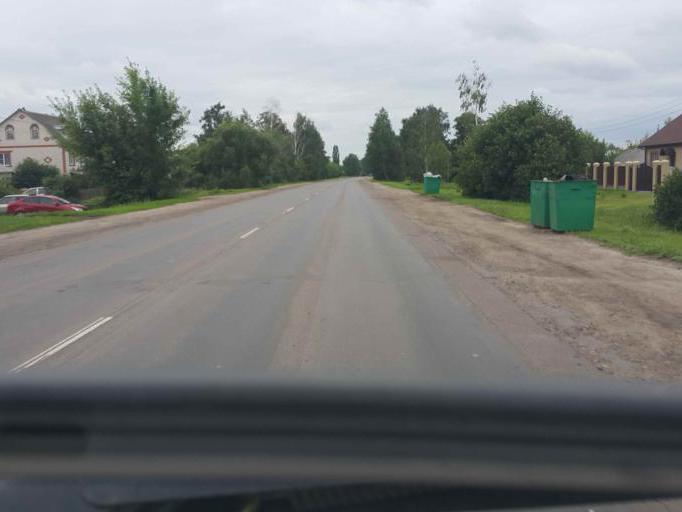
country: RU
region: Tambov
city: Zavoronezhskoye
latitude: 52.8860
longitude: 40.5568
